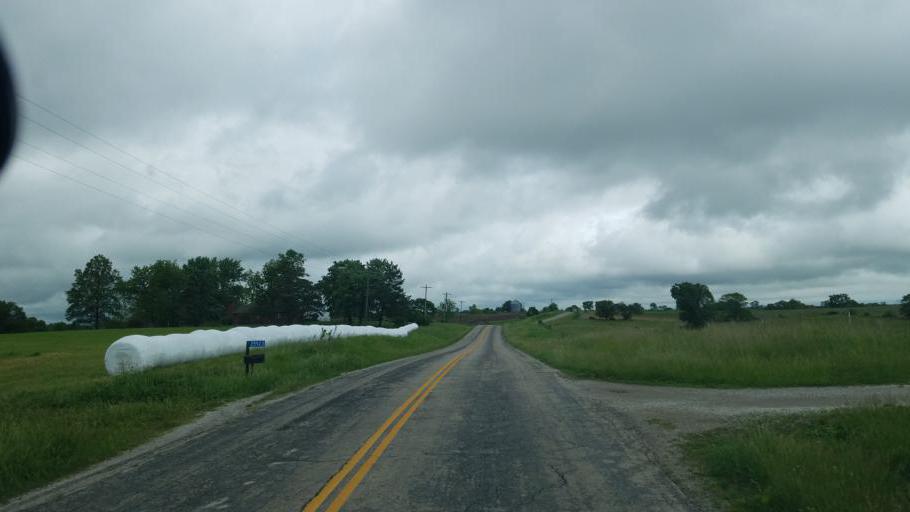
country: US
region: Missouri
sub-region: Mercer County
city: Princeton
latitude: 40.3437
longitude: -93.6828
